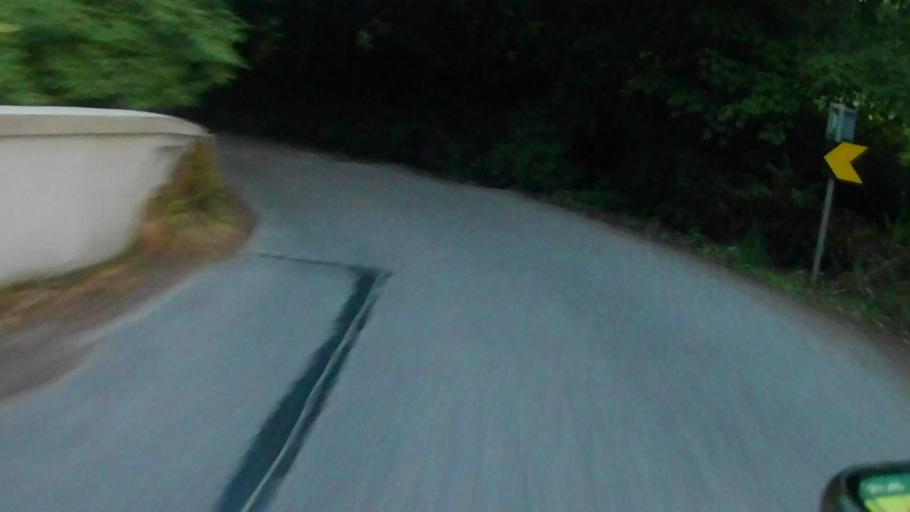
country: IE
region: Munster
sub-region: County Cork
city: Carrigtwohill
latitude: 51.9683
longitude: -8.2748
